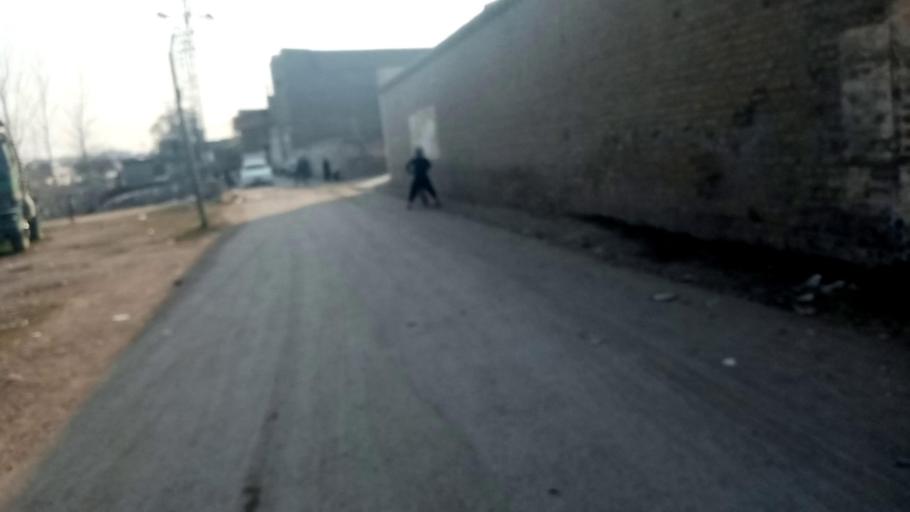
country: PK
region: Khyber Pakhtunkhwa
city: Peshawar
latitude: 34.0089
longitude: 71.4692
